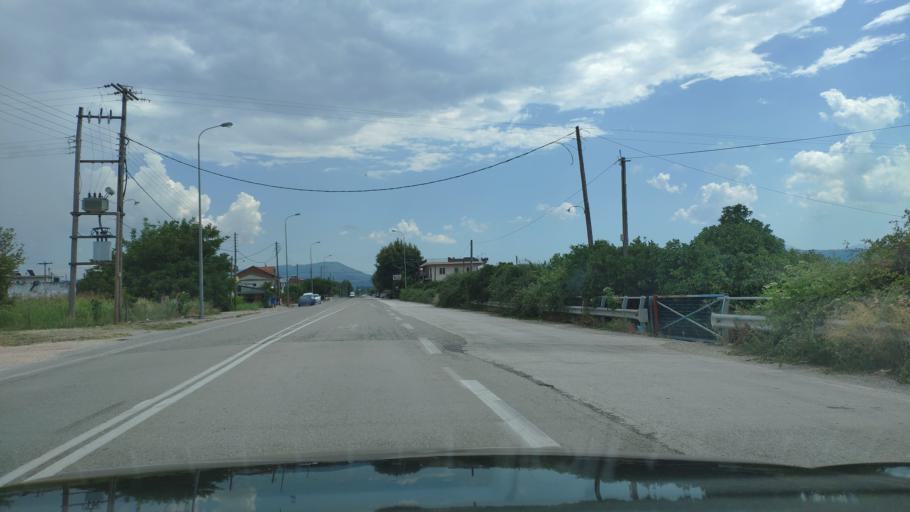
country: GR
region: West Greece
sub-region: Nomos Aitolias kai Akarnanias
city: Krikellos
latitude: 38.9504
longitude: 21.1761
